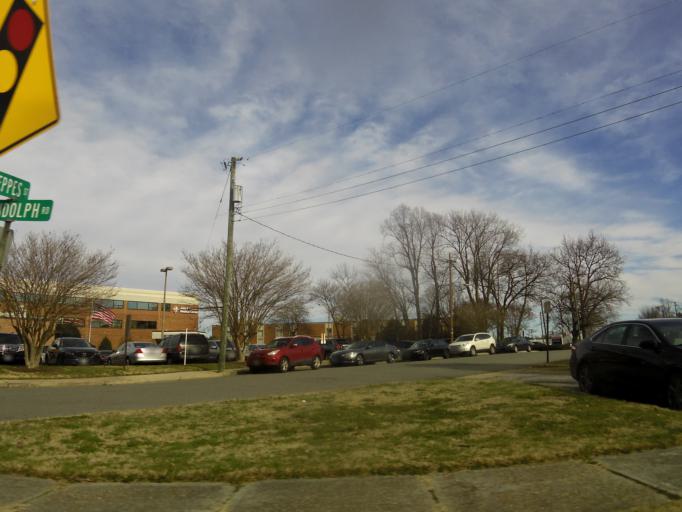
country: US
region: Virginia
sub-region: City of Hopewell
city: Hopewell
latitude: 37.3068
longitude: -77.2911
